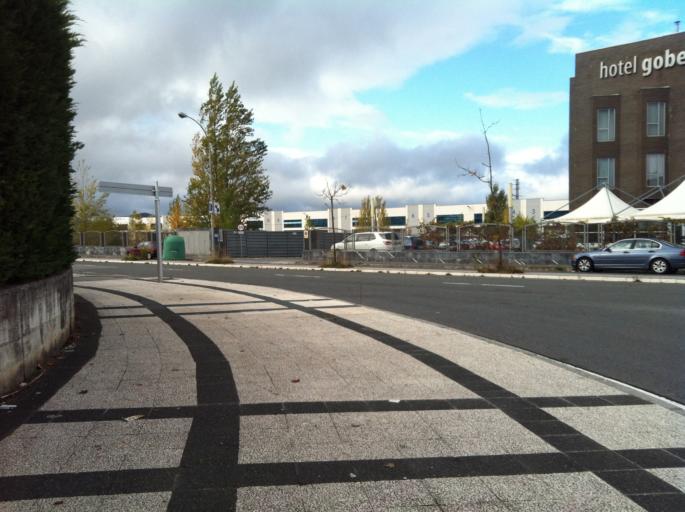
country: ES
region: Basque Country
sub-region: Provincia de Alava
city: Gasteiz / Vitoria
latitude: 42.8560
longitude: -2.7112
